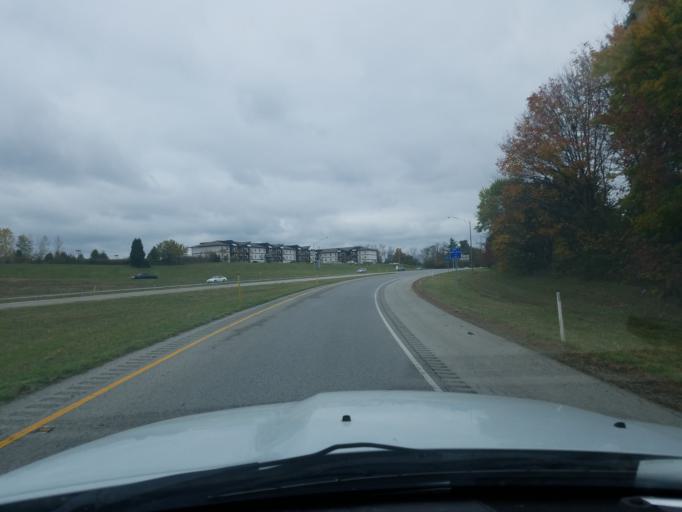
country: US
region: Indiana
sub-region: Floyd County
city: New Albany
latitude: 38.3366
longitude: -85.8156
